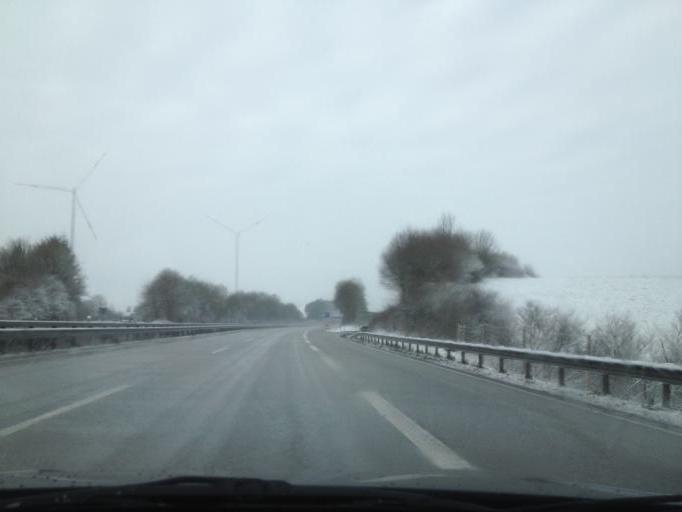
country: DE
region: Rheinland-Pfalz
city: Walshausen
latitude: 49.2143
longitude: 7.5007
